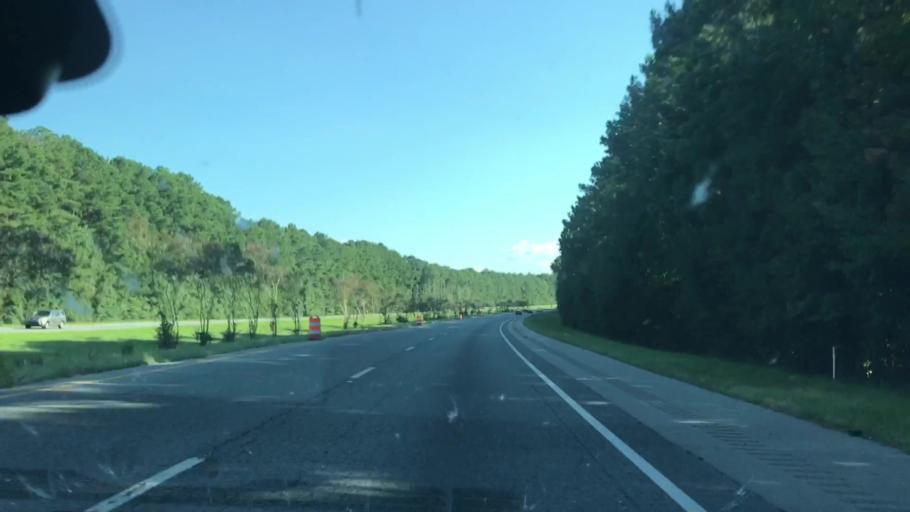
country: US
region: Georgia
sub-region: Harris County
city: Hamilton
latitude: 32.7582
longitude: -85.0167
